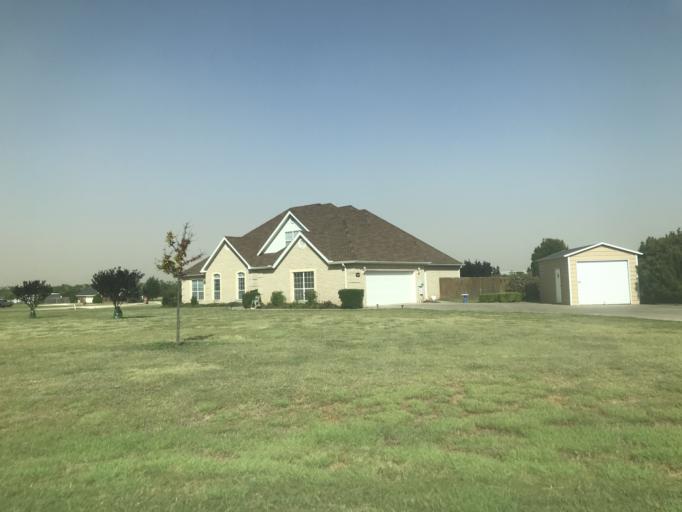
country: US
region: Texas
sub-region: Taylor County
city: Potosi
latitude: 32.3391
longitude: -99.7134
